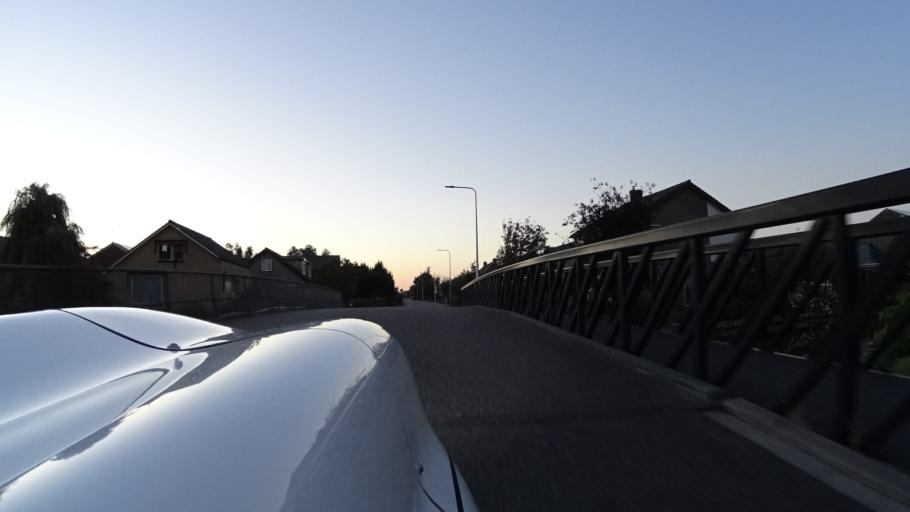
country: NL
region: South Holland
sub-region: Gemeente Kaag en Braassem
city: Oude Wetering
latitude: 52.1895
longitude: 4.6205
